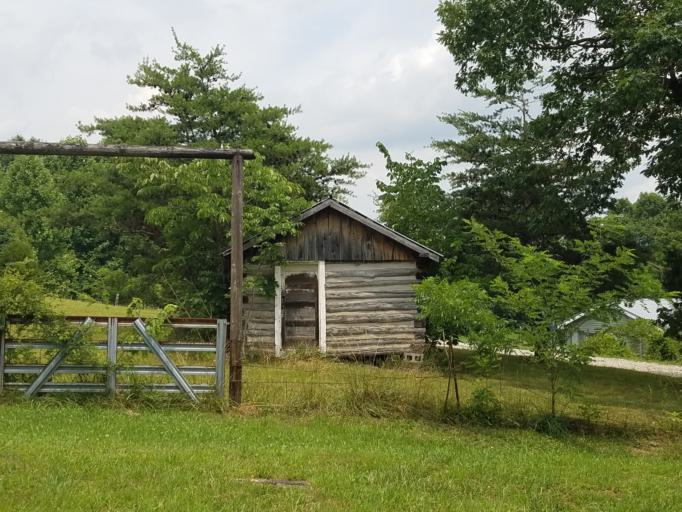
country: US
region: Kentucky
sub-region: Grayson County
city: Leitchfield
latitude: 37.3620
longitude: -86.1375
